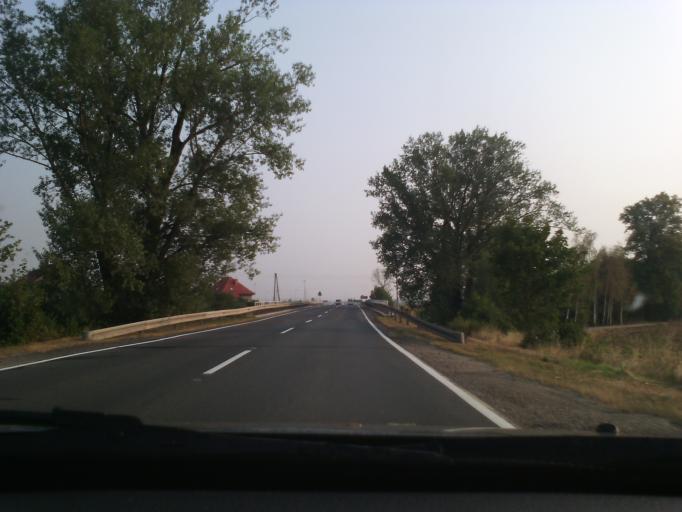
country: PL
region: Lower Silesian Voivodeship
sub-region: Powiat walbrzyski
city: Stare Bogaczowice
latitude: 50.9118
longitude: 16.2508
